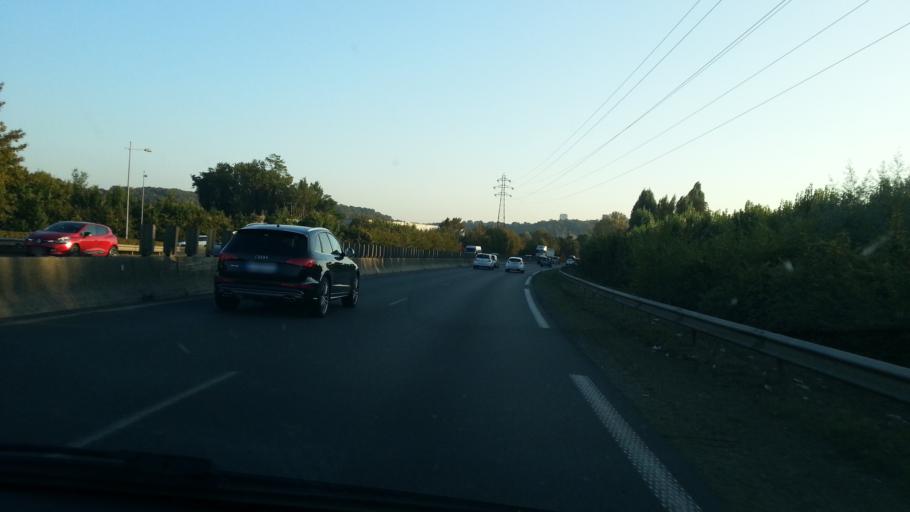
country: FR
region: Picardie
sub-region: Departement de l'Oise
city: Villers-Saint-Paul
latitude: 49.2748
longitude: 2.4860
